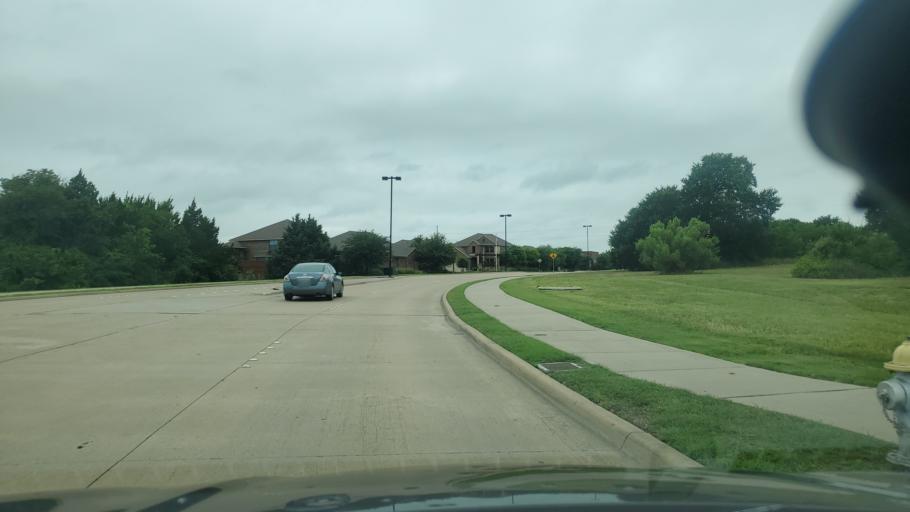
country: US
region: Texas
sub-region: Dallas County
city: Sachse
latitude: 32.9561
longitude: -96.6332
